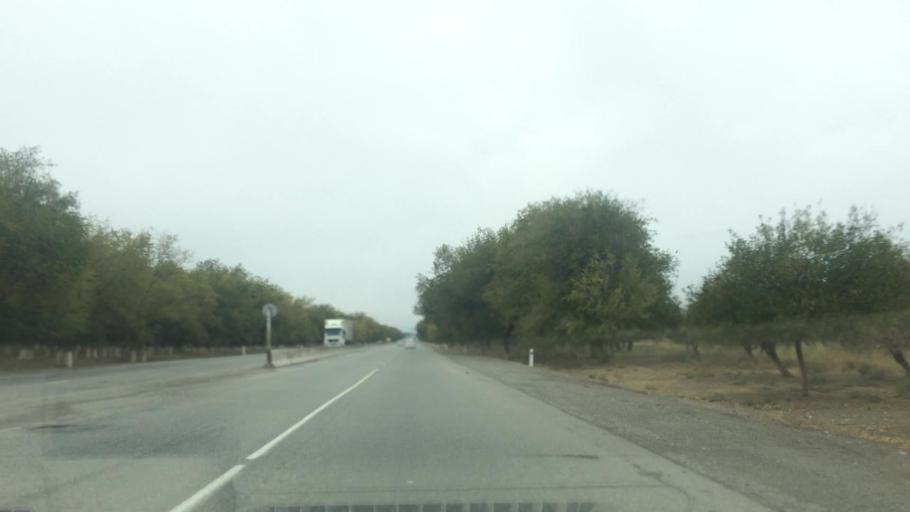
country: UZ
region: Samarqand
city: Bulung'ur
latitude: 39.7998
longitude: 67.3410
